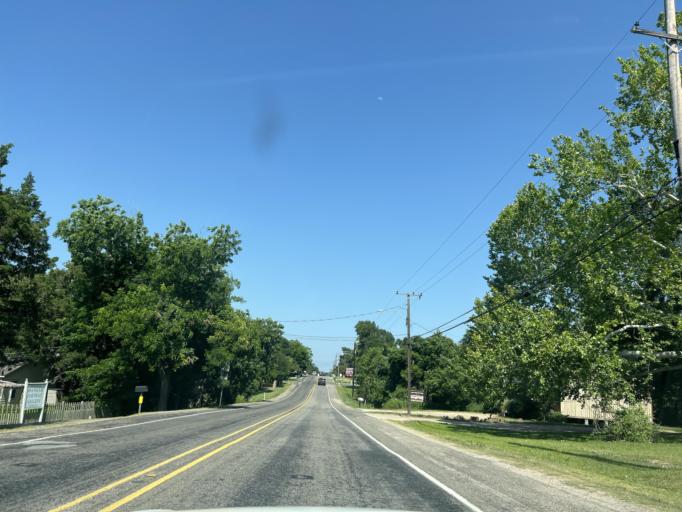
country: US
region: Texas
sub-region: Washington County
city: Brenham
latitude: 30.1659
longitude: -96.4216
